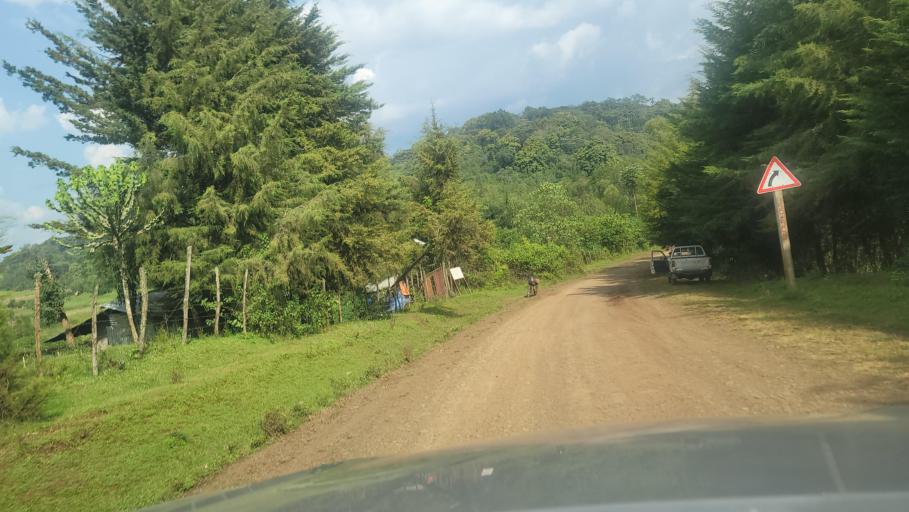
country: ET
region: Oromiya
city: Agaro
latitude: 7.7239
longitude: 36.2577
